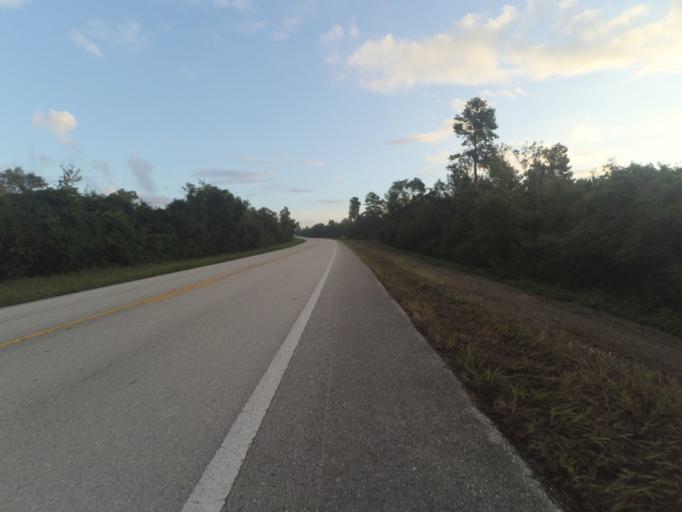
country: US
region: Florida
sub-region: Lake County
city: Astor
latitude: 29.2202
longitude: -81.6462
